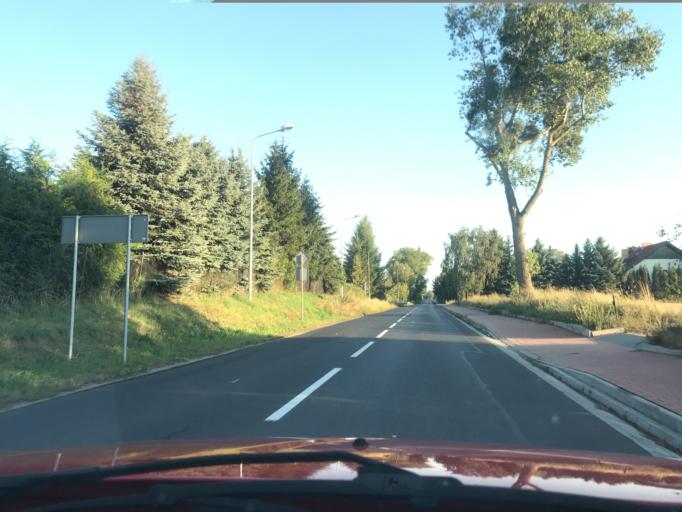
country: PL
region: Greater Poland Voivodeship
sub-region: Powiat poznanski
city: Tarnowo Podgorne
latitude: 52.4242
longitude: 16.7178
